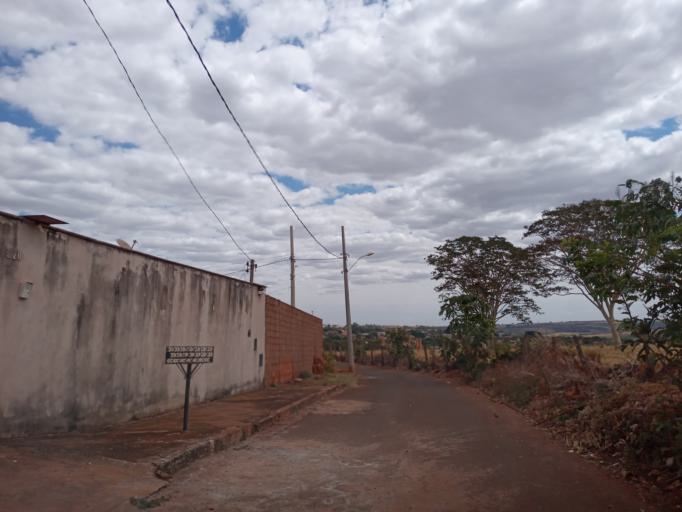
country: BR
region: Minas Gerais
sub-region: Ituiutaba
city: Ituiutaba
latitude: -18.9546
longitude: -49.4498
